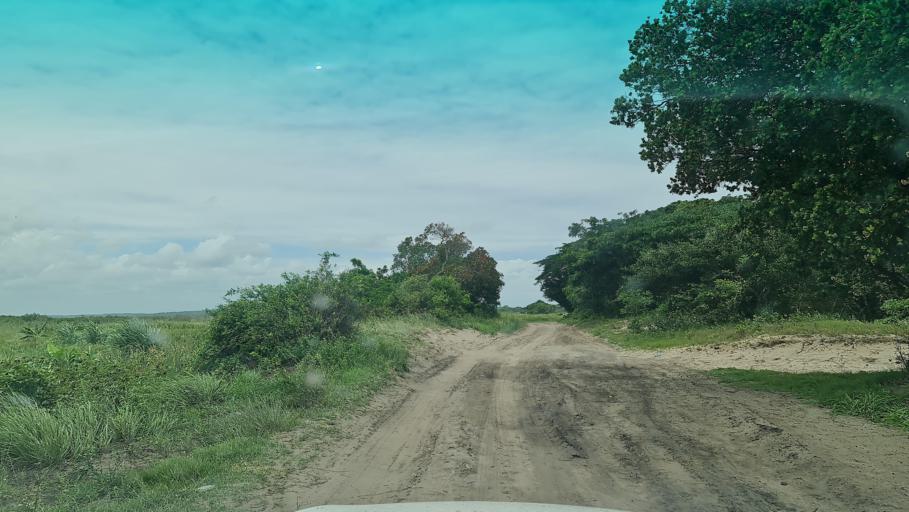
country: MZ
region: Maputo
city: Manhica
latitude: -25.5280
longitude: 32.8512
